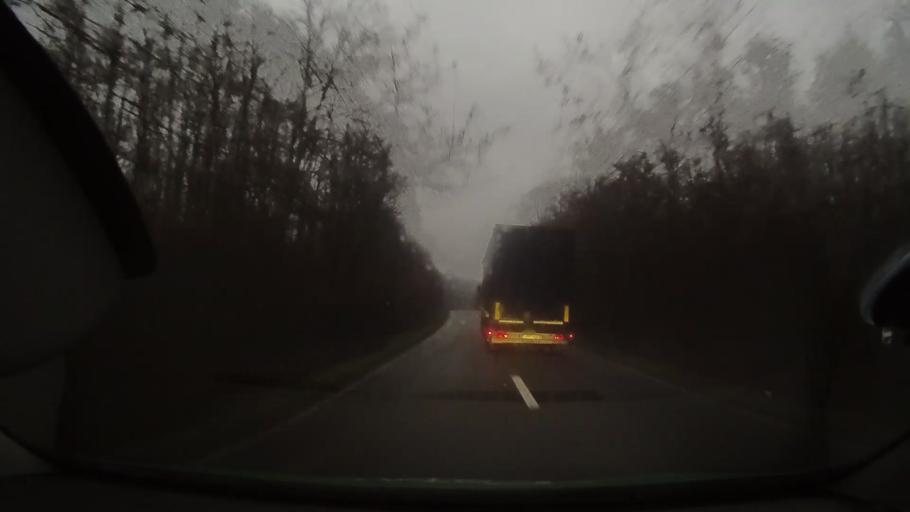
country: RO
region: Arad
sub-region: Comuna Beliu
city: Beliu
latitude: 46.5063
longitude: 21.9699
